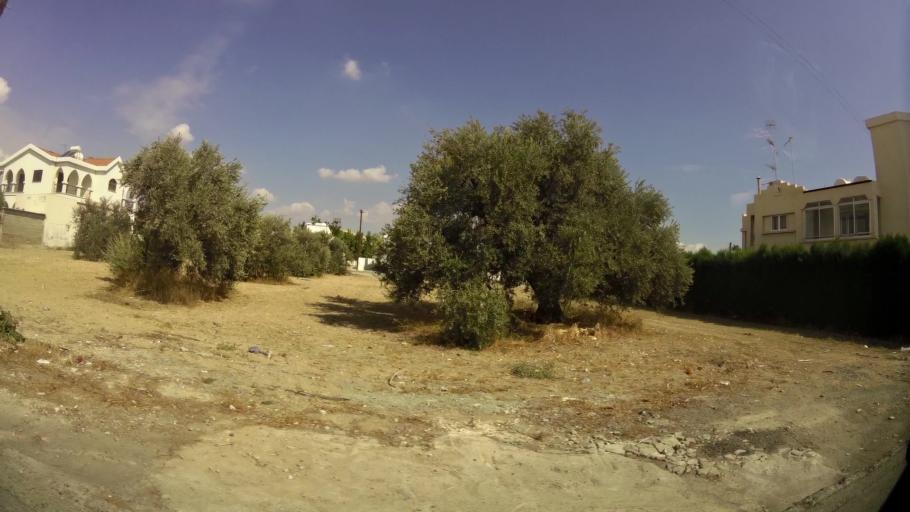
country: CY
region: Larnaka
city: Aradippou
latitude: 34.9403
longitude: 33.5903
